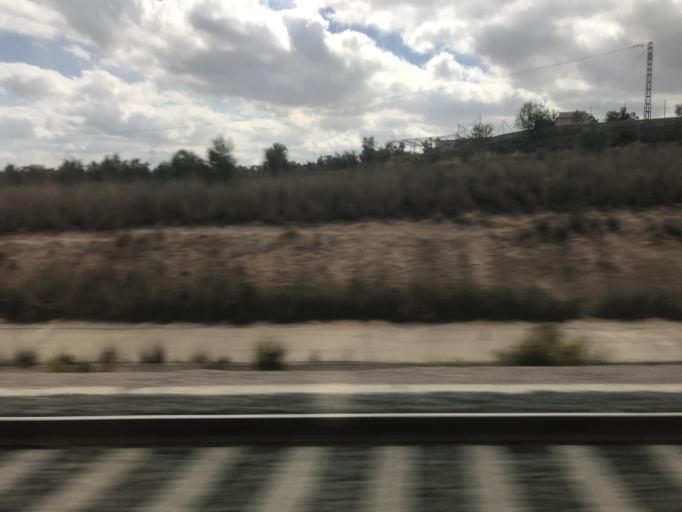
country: ES
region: Castille-La Mancha
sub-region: Provincia de Albacete
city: Almansa
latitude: 38.8853
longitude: -1.1411
